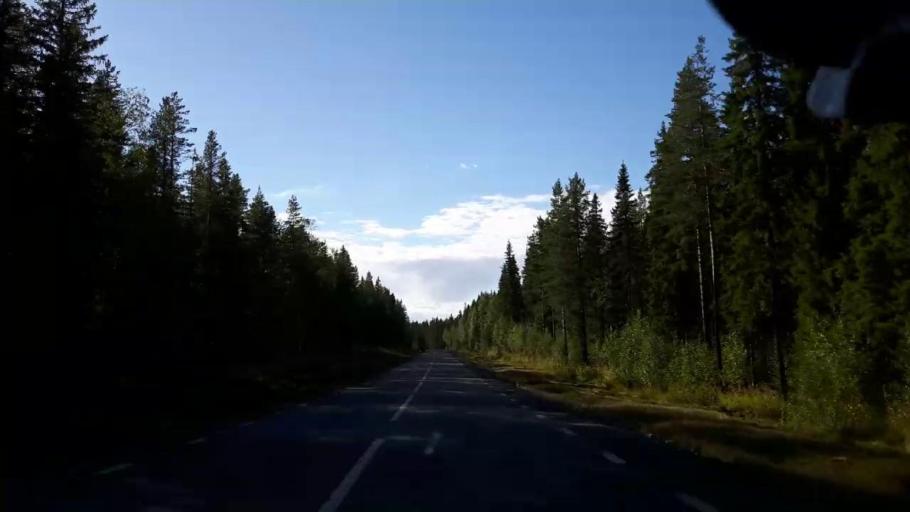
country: SE
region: Jaemtland
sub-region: Ragunda Kommun
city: Hammarstrand
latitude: 63.5367
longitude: 16.0323
